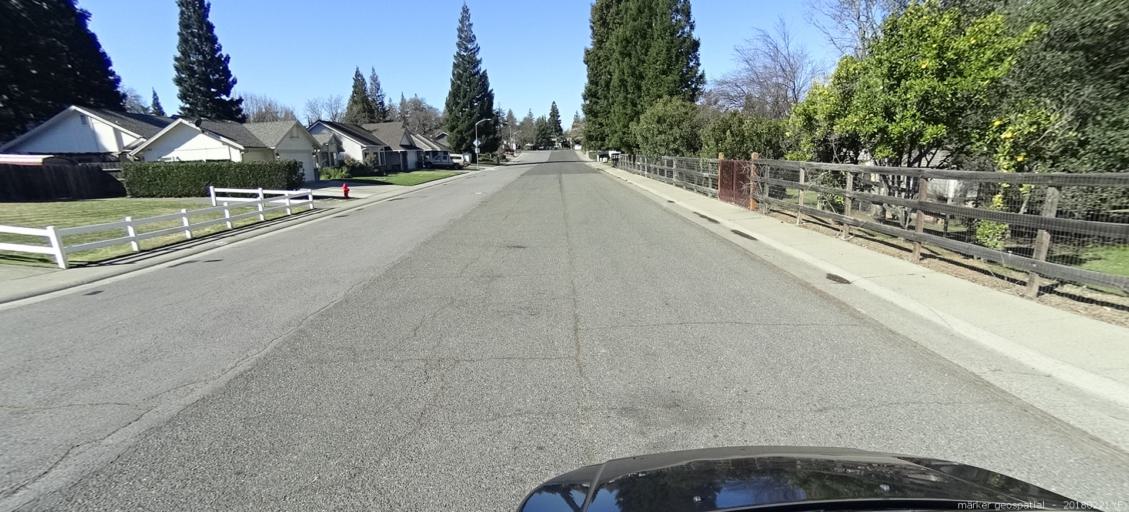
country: US
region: California
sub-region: Sacramento County
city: Orangevale
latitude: 38.6968
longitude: -121.2421
